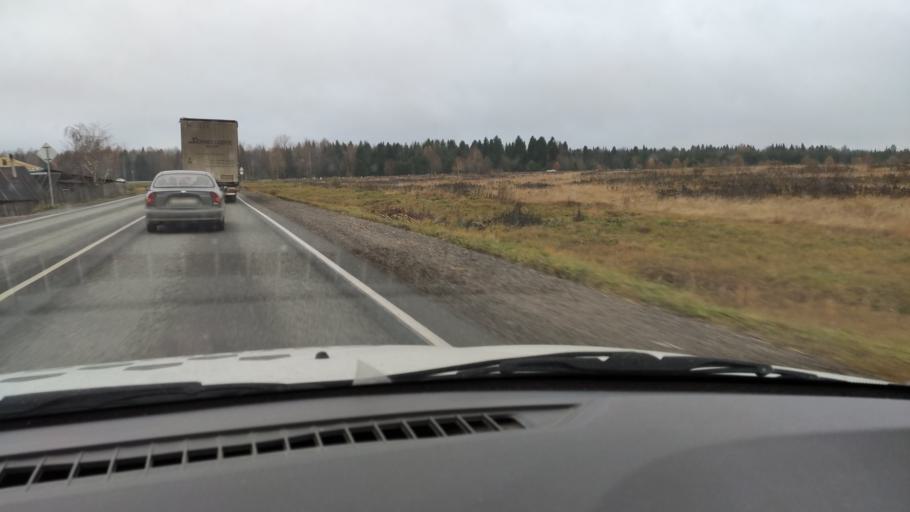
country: RU
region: Kirov
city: Omutninsk
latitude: 58.6930
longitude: 52.2035
